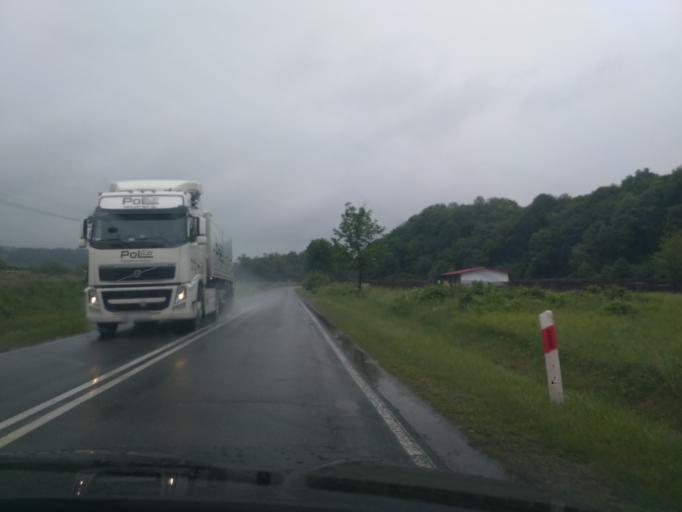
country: PL
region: Subcarpathian Voivodeship
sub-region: Powiat strzyzowski
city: Frysztak
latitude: 49.8204
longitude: 21.6293
